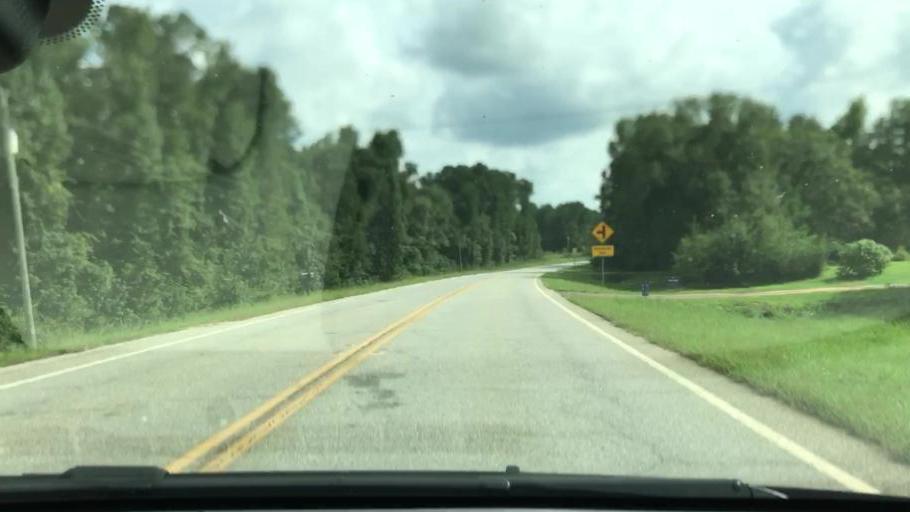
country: US
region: Georgia
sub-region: Clay County
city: Fort Gaines
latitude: 31.6723
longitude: -85.0466
